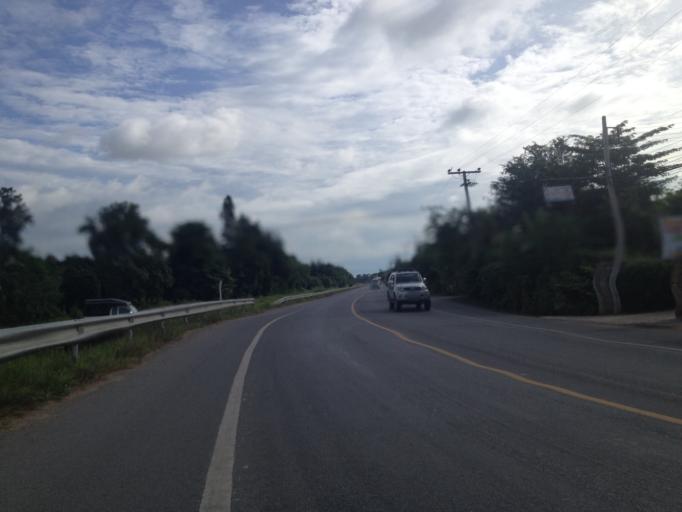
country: TH
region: Chiang Mai
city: San Pa Tong
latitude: 18.6515
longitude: 98.8563
